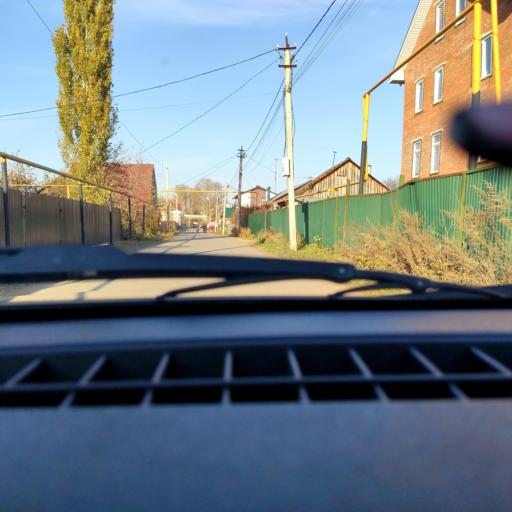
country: RU
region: Bashkortostan
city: Ufa
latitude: 54.6865
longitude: 55.9584
